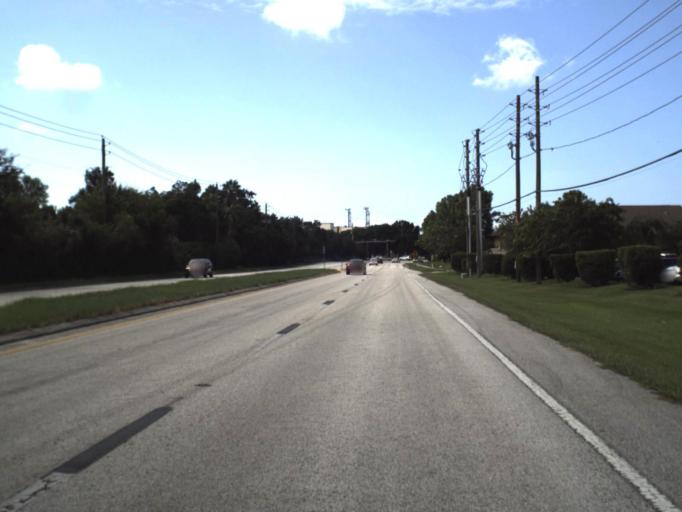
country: US
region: Florida
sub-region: Pinellas County
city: Saint George
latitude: 28.0667
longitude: -82.7054
